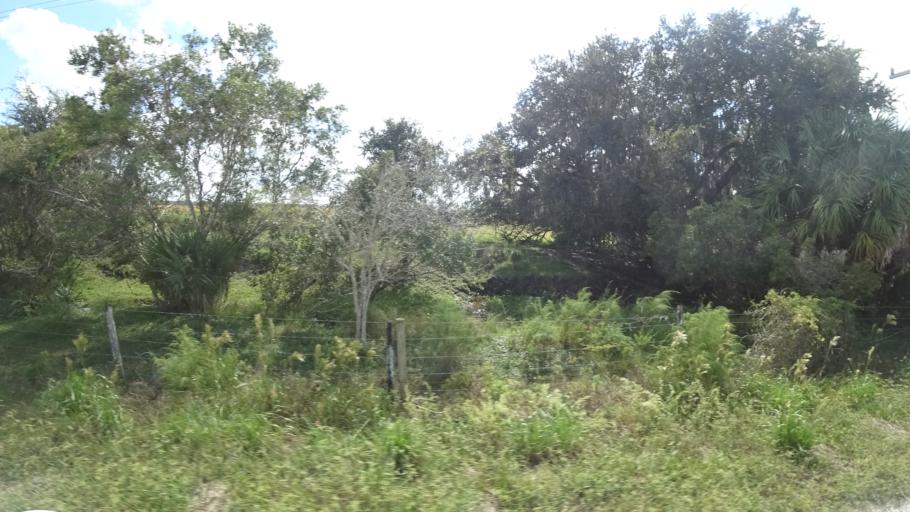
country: US
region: Florida
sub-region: Sarasota County
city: North Port
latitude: 27.2080
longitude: -82.1112
